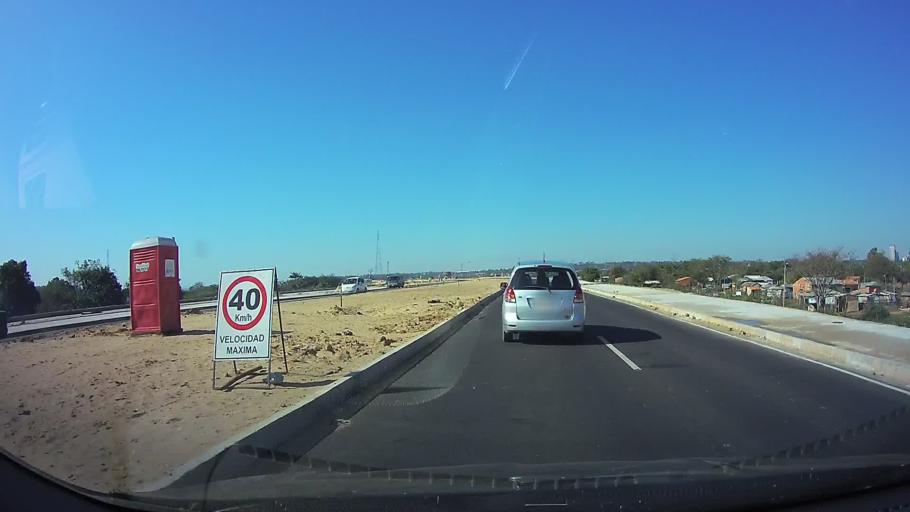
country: PY
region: Asuncion
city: Asuncion
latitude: -25.2493
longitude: -57.6027
